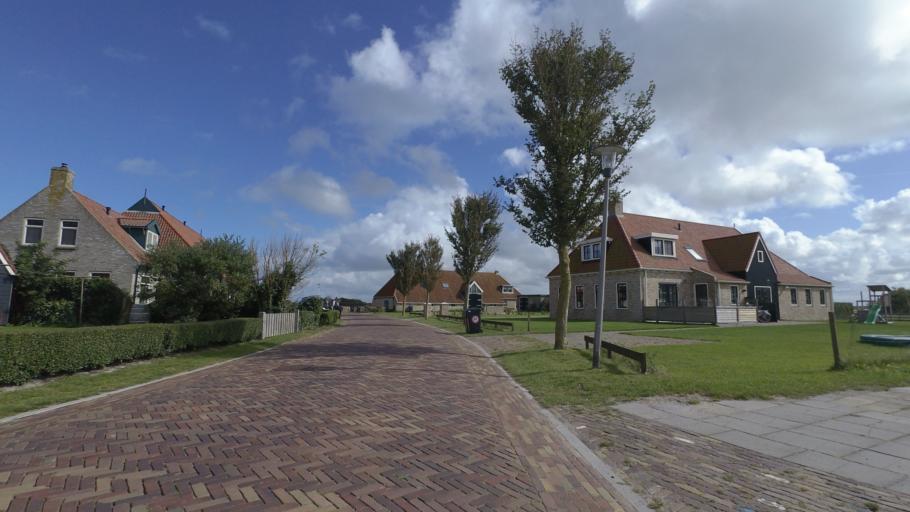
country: NL
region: Friesland
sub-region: Gemeente Ameland
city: Nes
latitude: 53.4485
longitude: 5.8046
